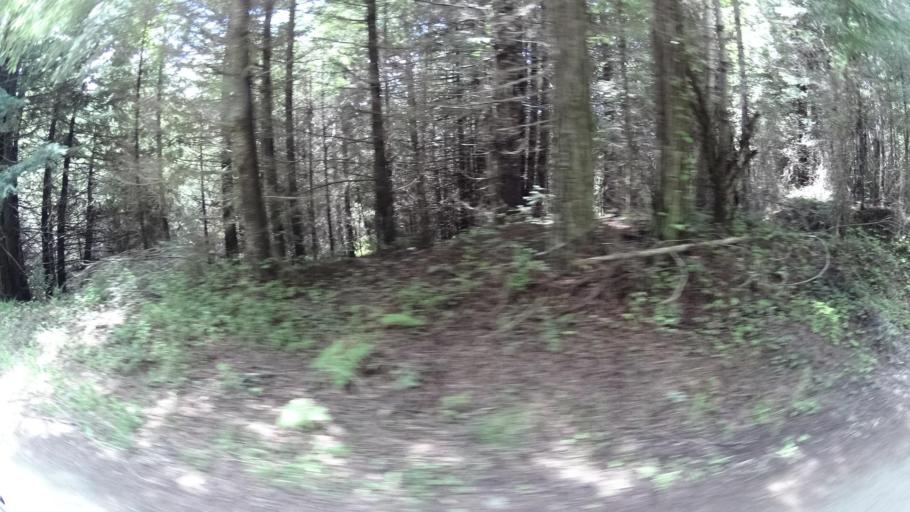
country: US
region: California
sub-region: Humboldt County
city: Blue Lake
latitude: 40.8161
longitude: -123.8904
